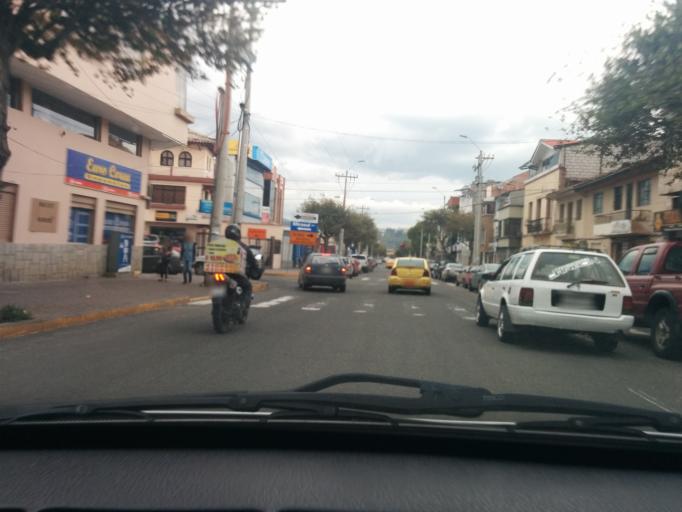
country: EC
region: Azuay
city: Cuenca
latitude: -2.8980
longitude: -78.9958
